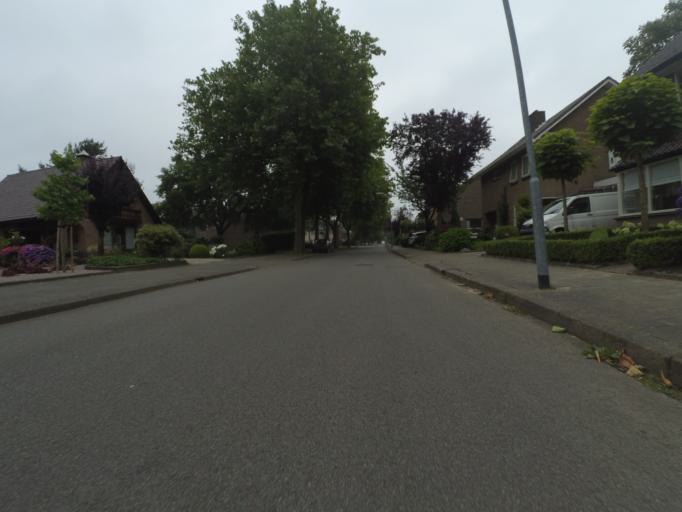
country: NL
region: Gelderland
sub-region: Gemeente Barneveld
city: Barneveld
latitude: 52.1336
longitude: 5.5730
